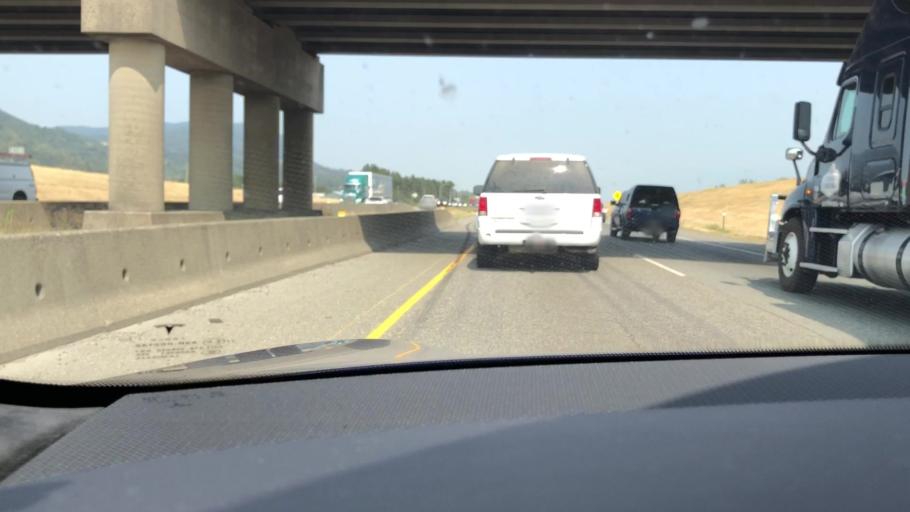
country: CA
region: British Columbia
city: Abbotsford
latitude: 49.0391
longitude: -122.2184
